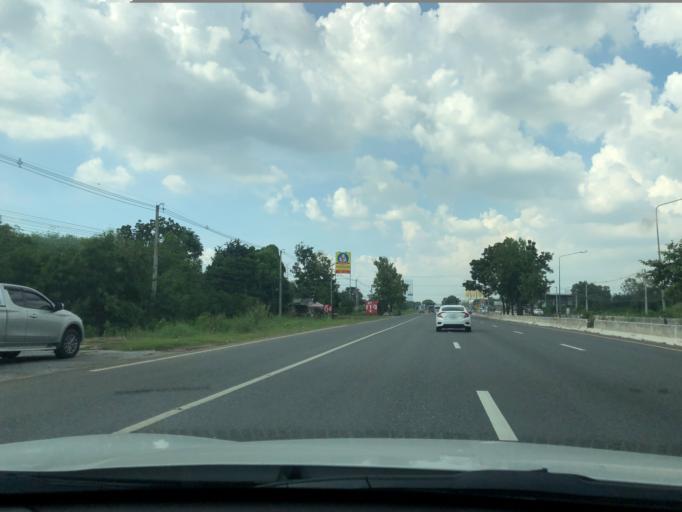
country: TH
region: Nakhon Sawan
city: Krok Phra
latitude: 15.5871
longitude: 100.1238
